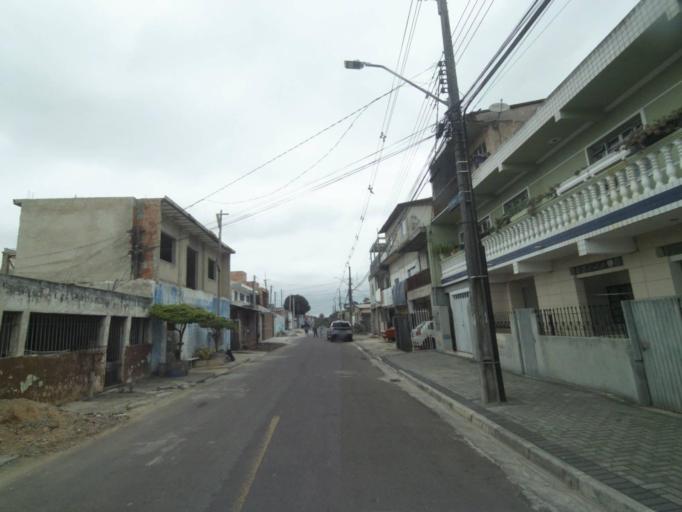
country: BR
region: Parana
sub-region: Araucaria
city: Araucaria
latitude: -25.5321
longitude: -49.3363
